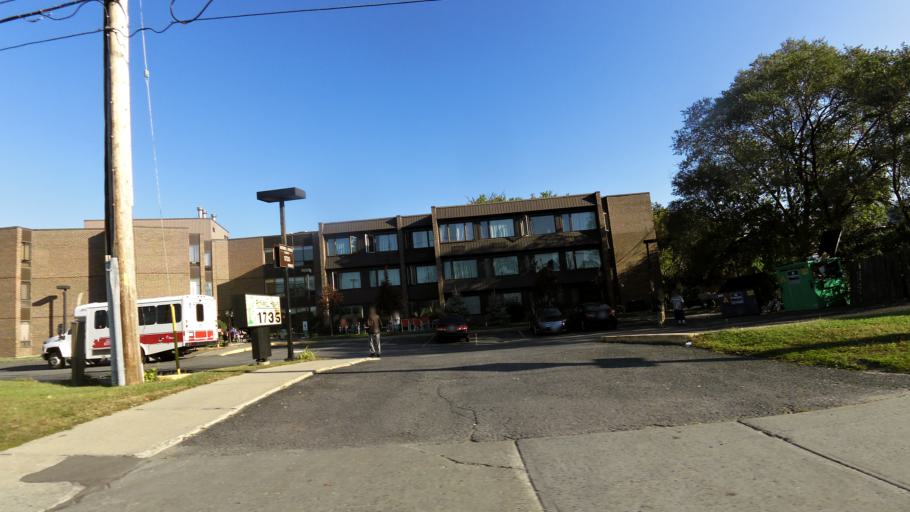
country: CA
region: Ontario
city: Ottawa
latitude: 45.4460
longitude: -75.6095
